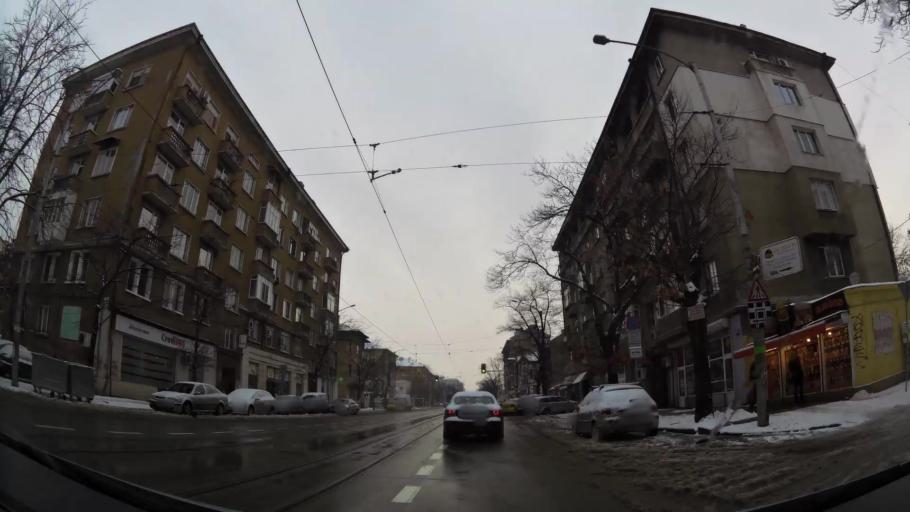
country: BG
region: Sofia-Capital
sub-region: Stolichna Obshtina
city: Sofia
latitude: 42.6999
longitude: 23.3014
